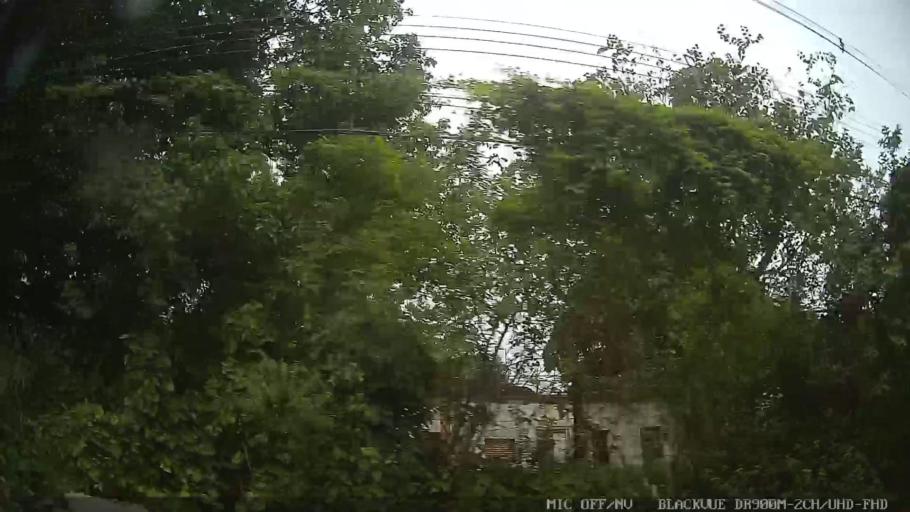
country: BR
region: Sao Paulo
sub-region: Pedreira
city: Pedreira
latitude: -22.6879
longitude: -46.8805
